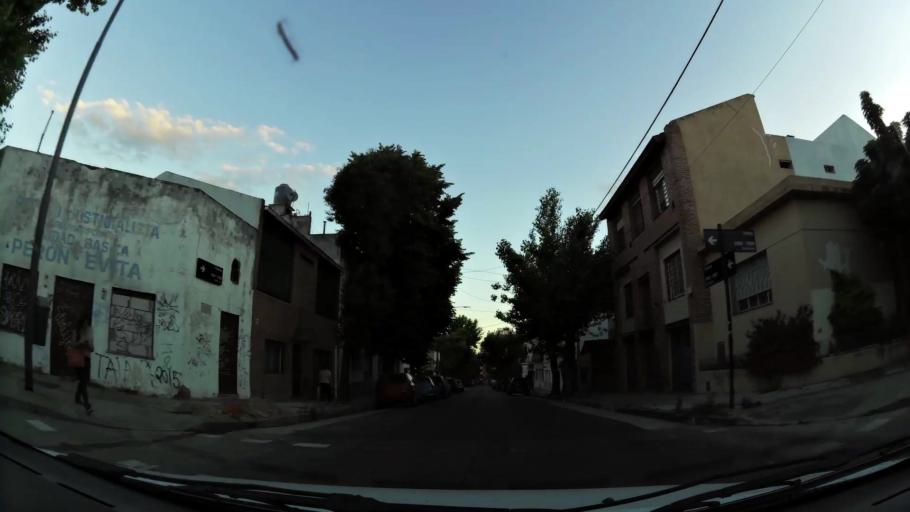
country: AR
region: Buenos Aires F.D.
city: Colegiales
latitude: -34.5478
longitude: -58.4751
